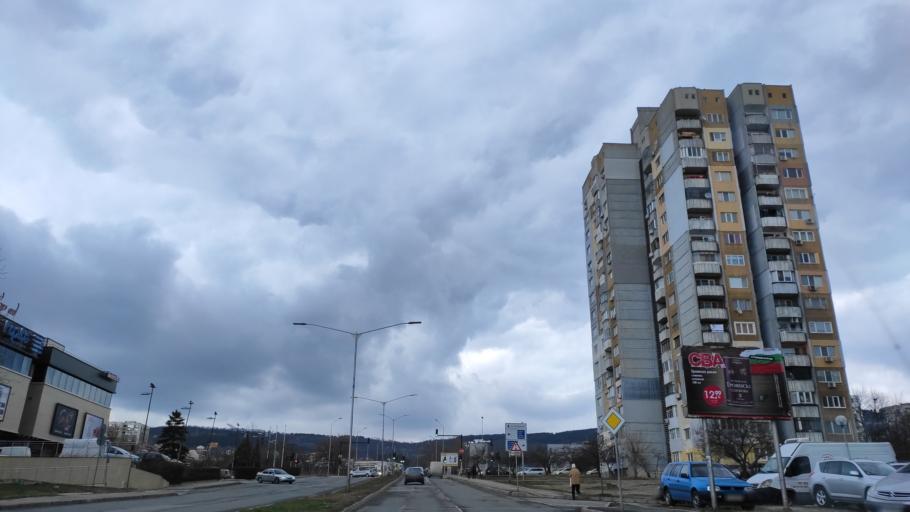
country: BG
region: Varna
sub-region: Obshtina Varna
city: Varna
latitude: 43.2330
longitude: 27.8801
